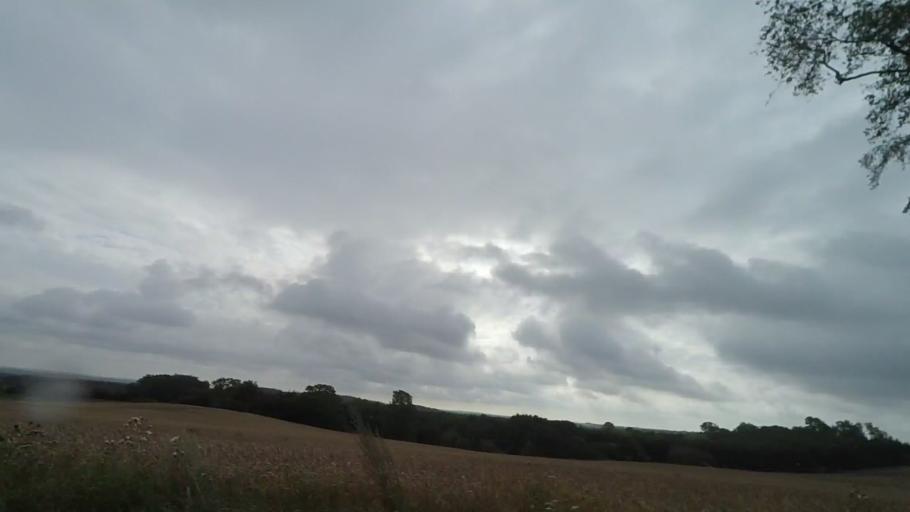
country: DK
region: Central Jutland
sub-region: Syddjurs Kommune
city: Ronde
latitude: 56.3260
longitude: 10.4587
